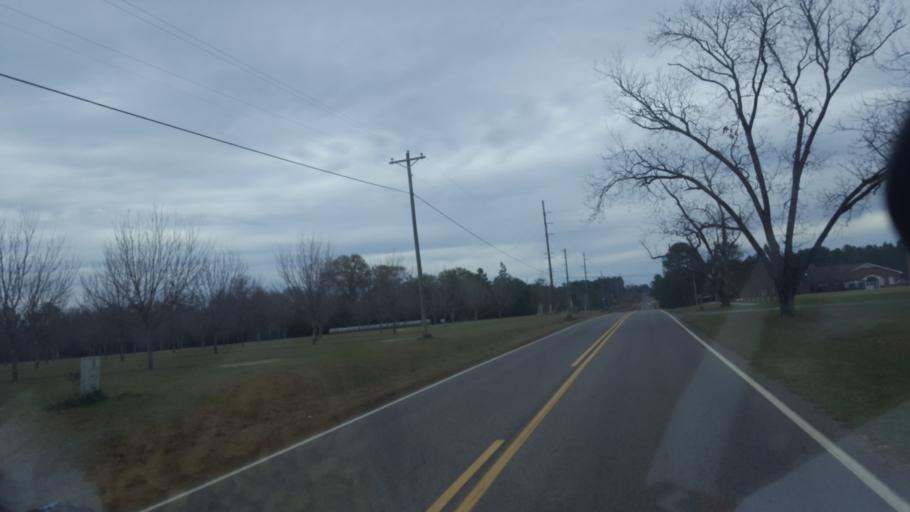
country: US
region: Georgia
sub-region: Ben Hill County
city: Fitzgerald
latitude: 31.7436
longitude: -83.2672
